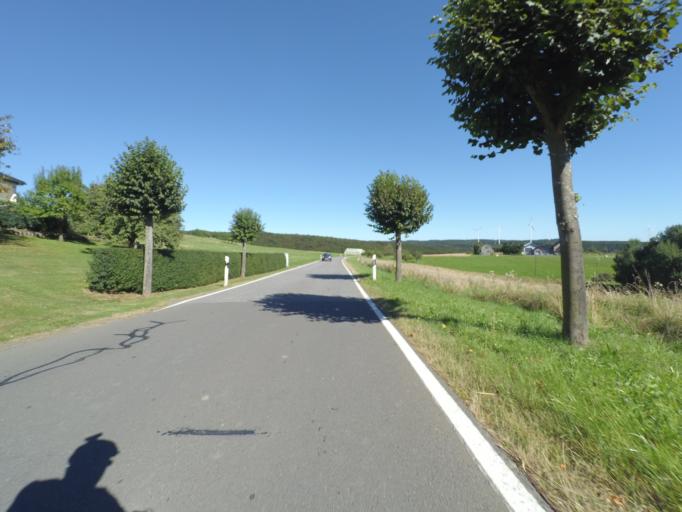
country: DE
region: Rheinland-Pfalz
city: Boxberg
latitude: 50.2729
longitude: 6.8772
